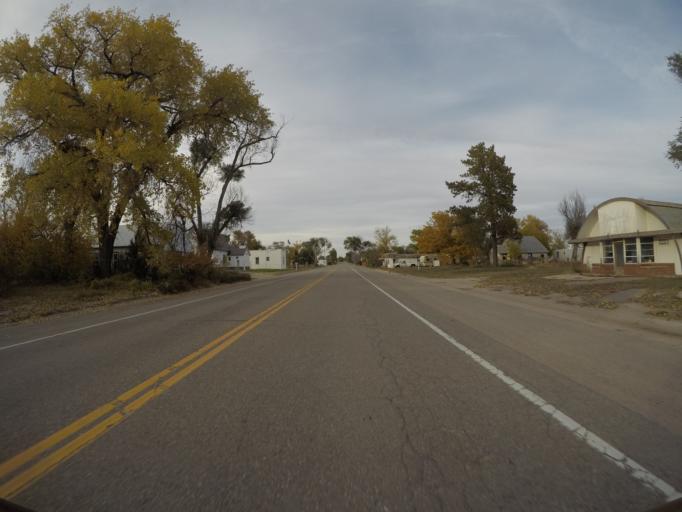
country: US
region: Colorado
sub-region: Yuma County
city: Yuma
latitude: 39.6628
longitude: -102.8510
